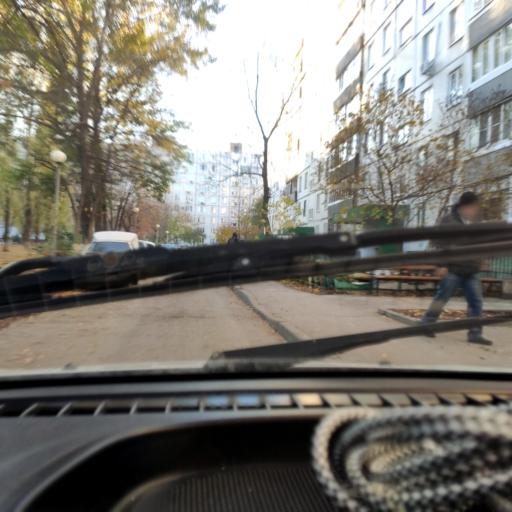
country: RU
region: Samara
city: Tol'yatti
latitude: 53.5083
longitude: 49.2787
